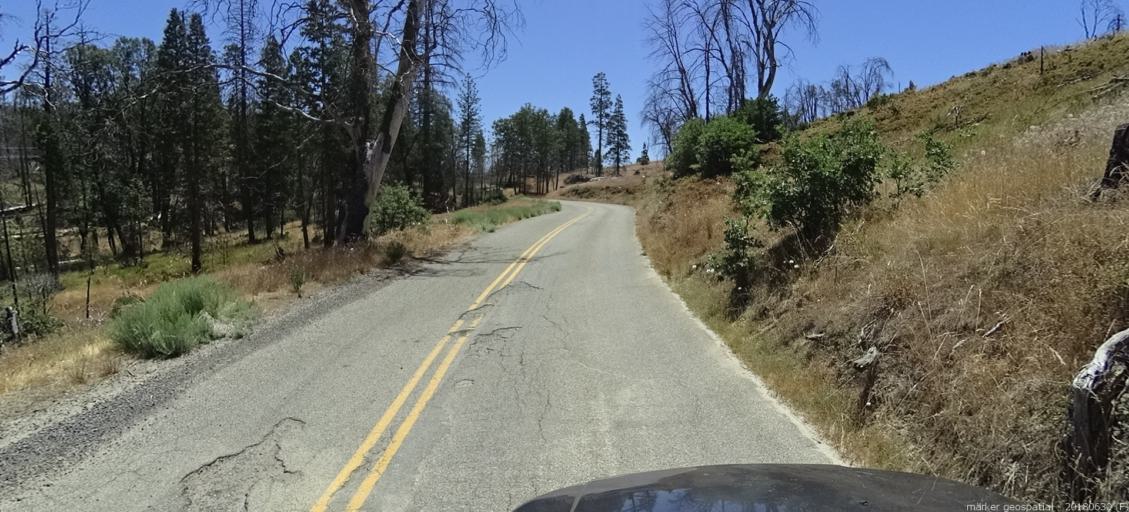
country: US
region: California
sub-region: Fresno County
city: Auberry
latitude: 37.2552
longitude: -119.3511
